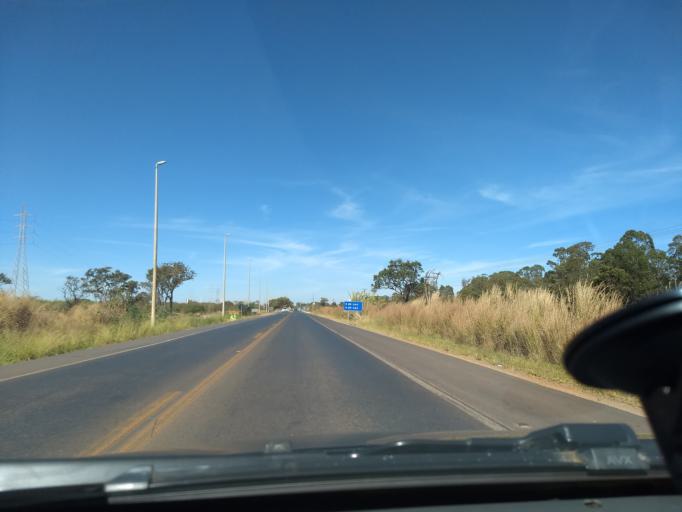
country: BR
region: Federal District
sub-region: Brasilia
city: Brasilia
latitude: -15.7852
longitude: -48.0505
